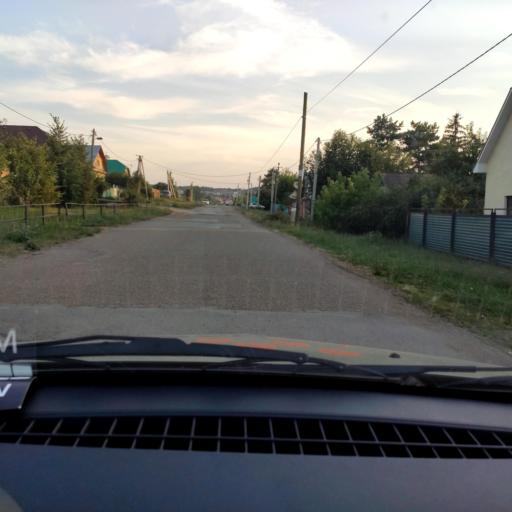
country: RU
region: Bashkortostan
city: Avdon
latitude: 54.5872
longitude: 55.6720
